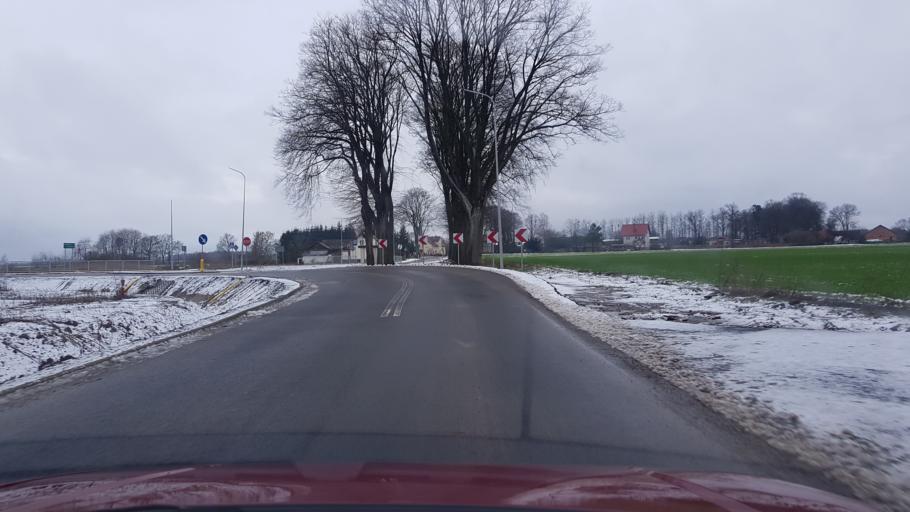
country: PL
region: West Pomeranian Voivodeship
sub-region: Powiat gryficki
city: Ploty
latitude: 53.8586
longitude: 15.3393
